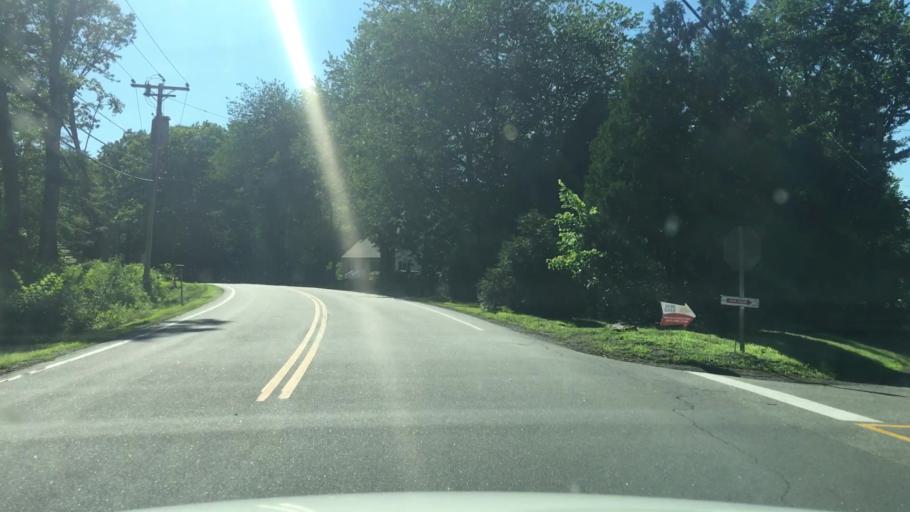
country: US
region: New Hampshire
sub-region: Rockingham County
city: Newmarket
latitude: 43.0376
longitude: -70.9488
